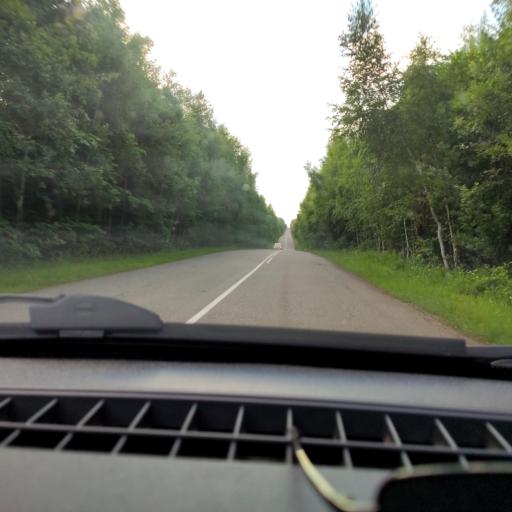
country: RU
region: Bashkortostan
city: Chishmy
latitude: 54.4401
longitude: 55.5593
